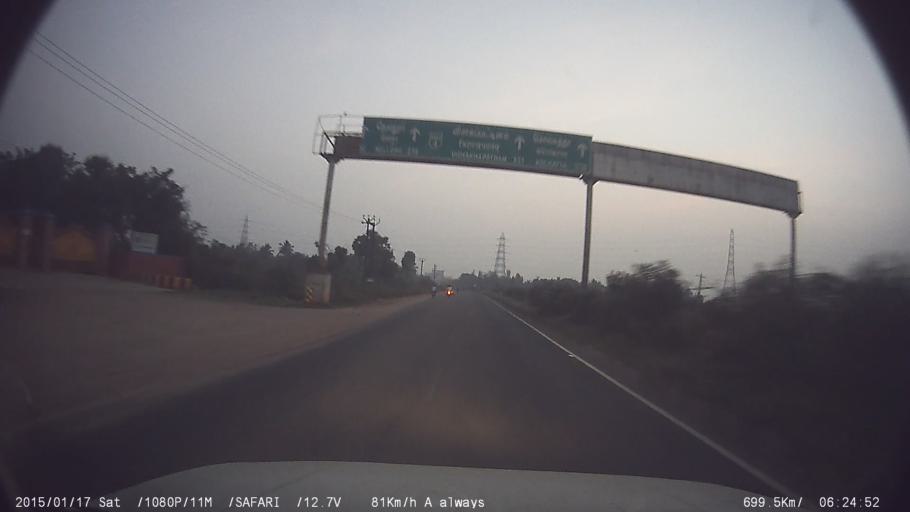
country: IN
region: Tamil Nadu
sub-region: Kancheepuram
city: Sriperumbudur
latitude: 12.9195
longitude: 79.8687
